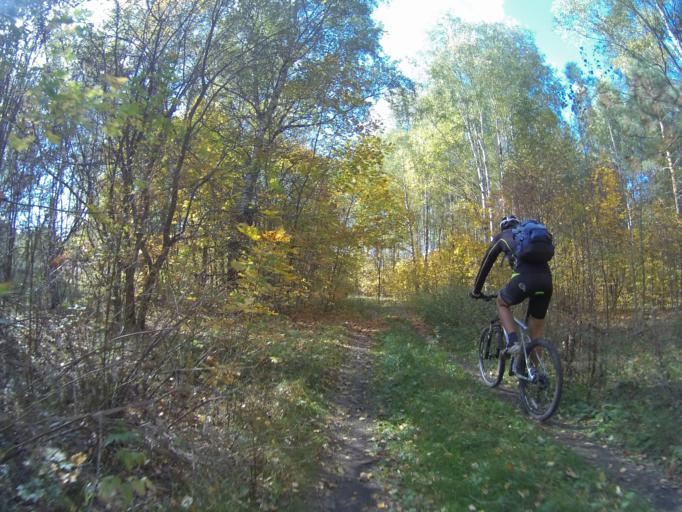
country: RU
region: Vladimir
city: Raduzhnyy
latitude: 55.8906
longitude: 40.2065
